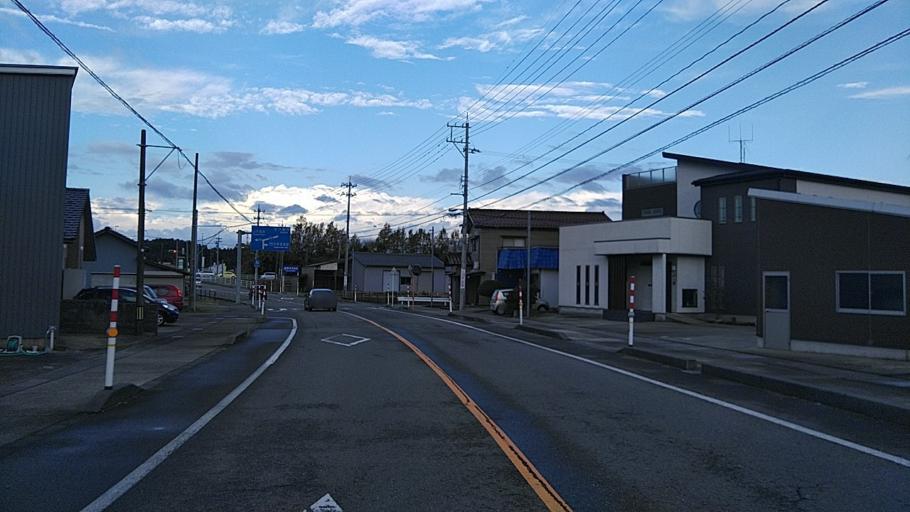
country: JP
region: Ishikawa
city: Komatsu
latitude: 36.2953
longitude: 136.3494
